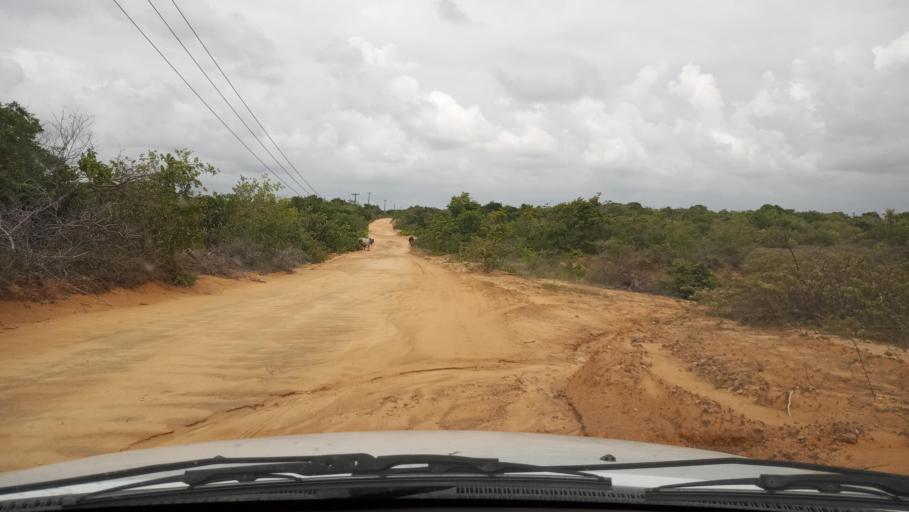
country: BR
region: Rio Grande do Norte
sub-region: Maxaranguape
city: Sao Miguel
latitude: -5.4831
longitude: -35.3049
